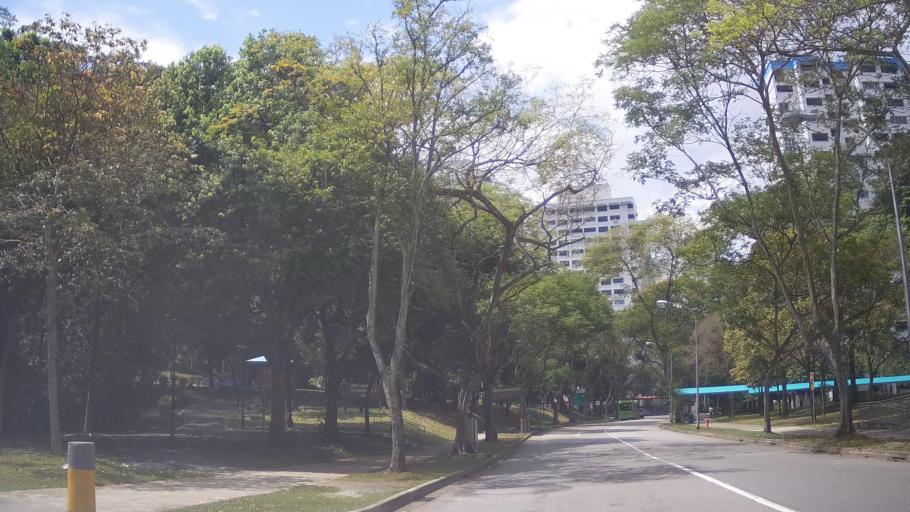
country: MY
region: Johor
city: Johor Bahru
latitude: 1.3829
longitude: 103.7663
